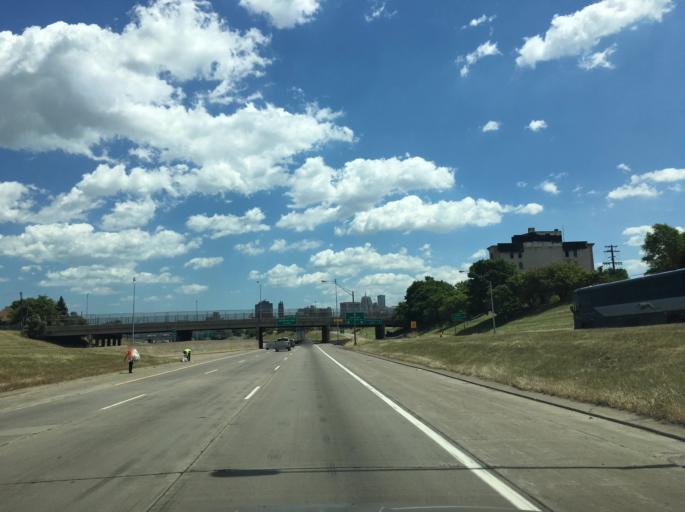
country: US
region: Michigan
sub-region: Wayne County
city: Detroit
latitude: 42.3323
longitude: -83.0794
